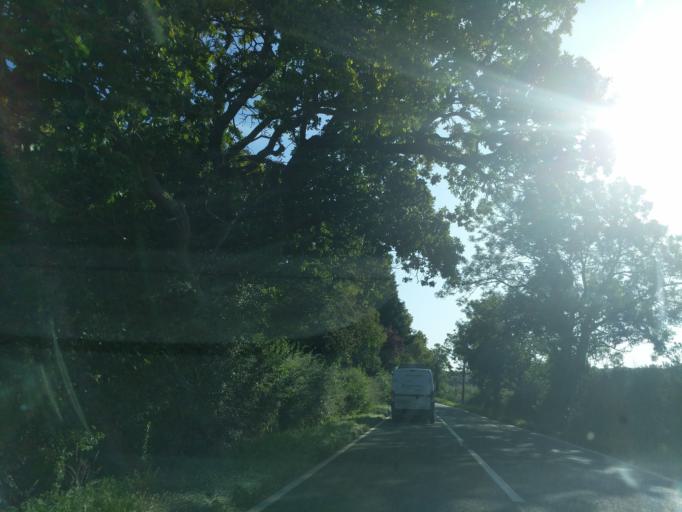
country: GB
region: England
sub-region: District of Rutland
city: Clipsham
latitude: 52.7993
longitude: -0.5645
